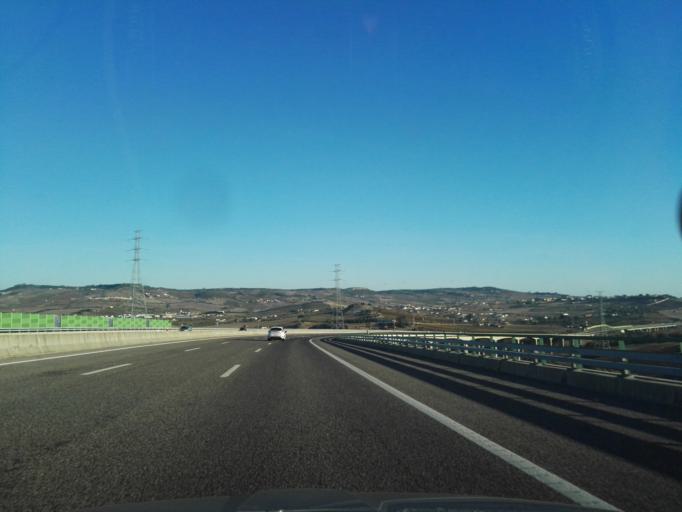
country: PT
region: Lisbon
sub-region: Arruda Dos Vinhos
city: Arruda dos Vinhos
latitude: 38.9752
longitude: -9.0593
